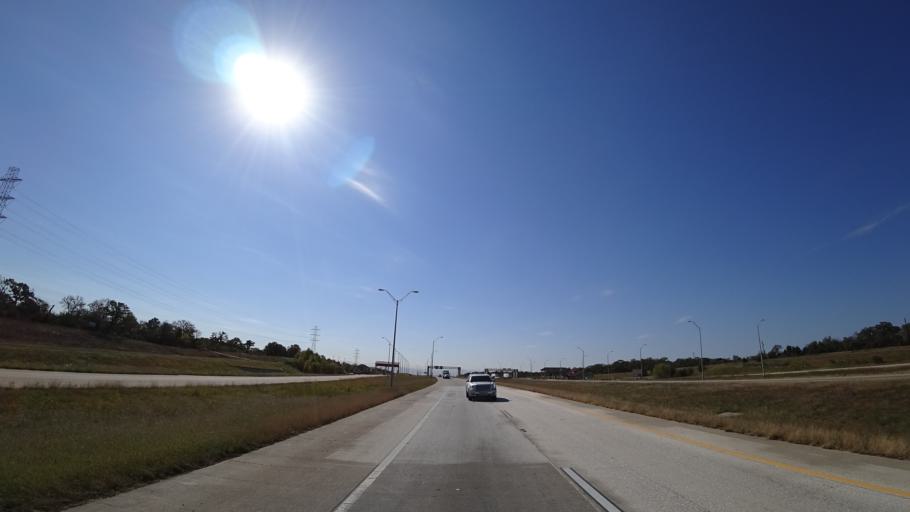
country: US
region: Texas
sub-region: Travis County
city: Hornsby Bend
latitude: 30.2717
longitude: -97.5925
